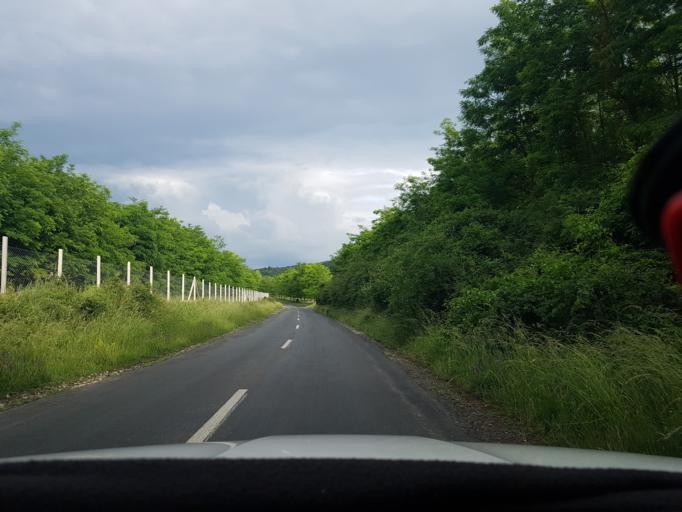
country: HU
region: Komarom-Esztergom
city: Nyergesujfalu
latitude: 47.7185
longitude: 18.5550
